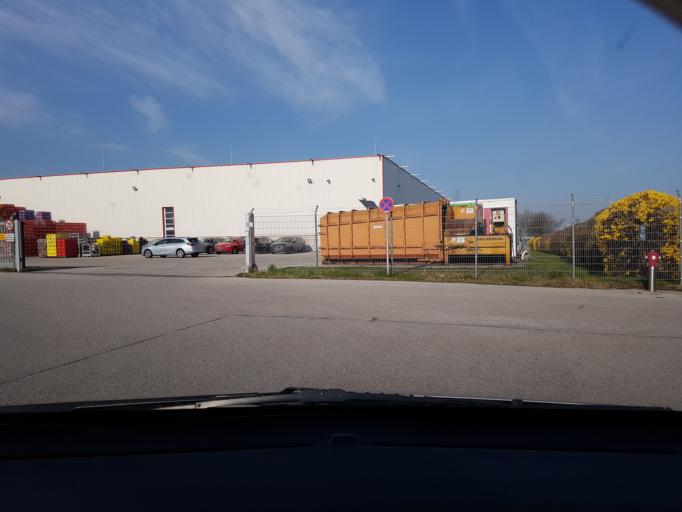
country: AT
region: Upper Austria
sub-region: Politischer Bezirk Linz-Land
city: Asten
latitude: 48.2242
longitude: 14.4090
